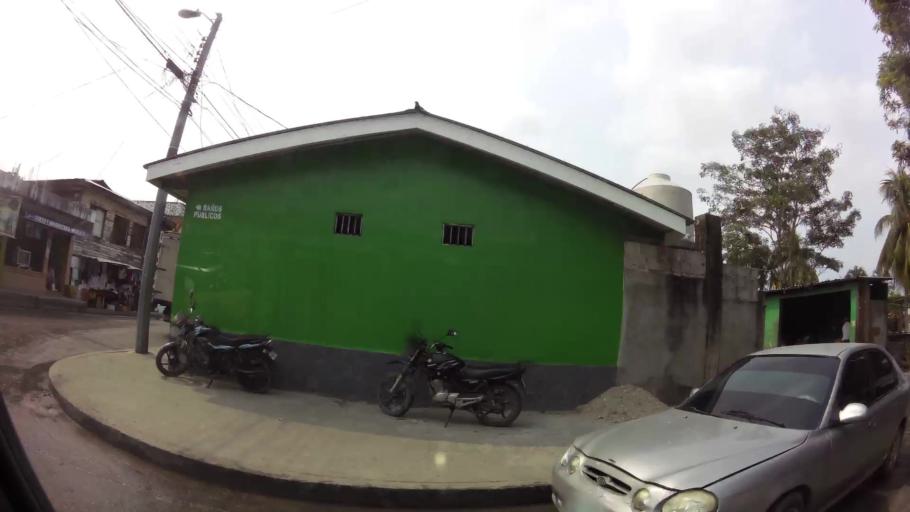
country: HN
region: Atlantida
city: Tela
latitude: 15.7852
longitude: -87.4505
